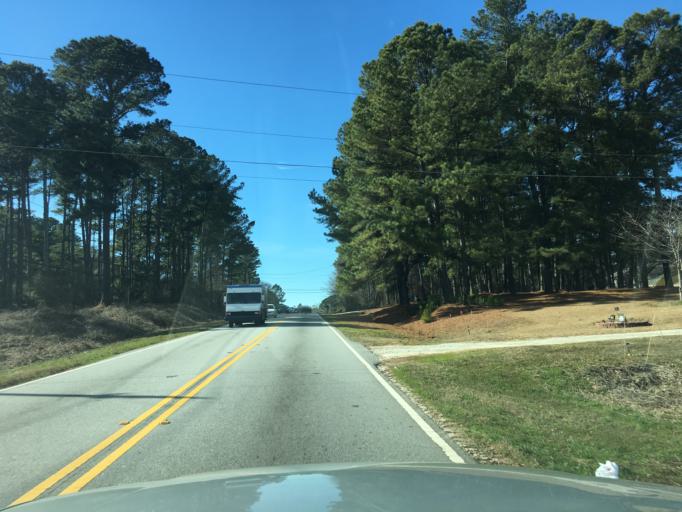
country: US
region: Georgia
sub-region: Rockdale County
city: Lakeview Estates
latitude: 33.6862
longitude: -84.0362
